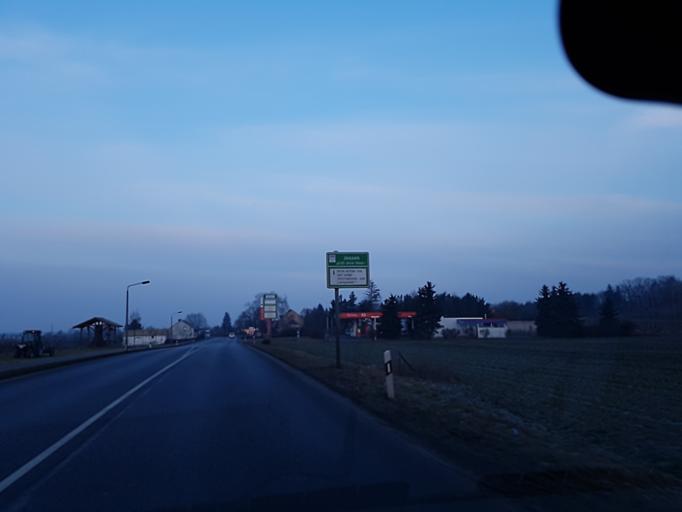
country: DE
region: Saxony-Anhalt
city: Jessen
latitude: 51.7970
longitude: 12.9890
